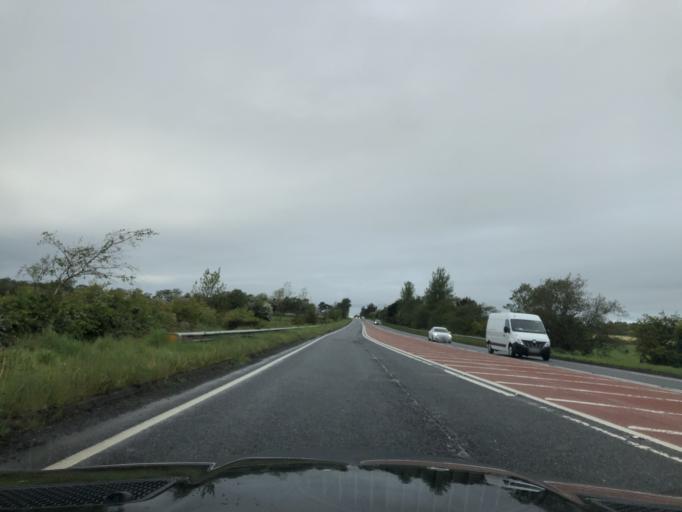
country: GB
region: Northern Ireland
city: Dunloy
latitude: 55.0322
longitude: -6.4010
